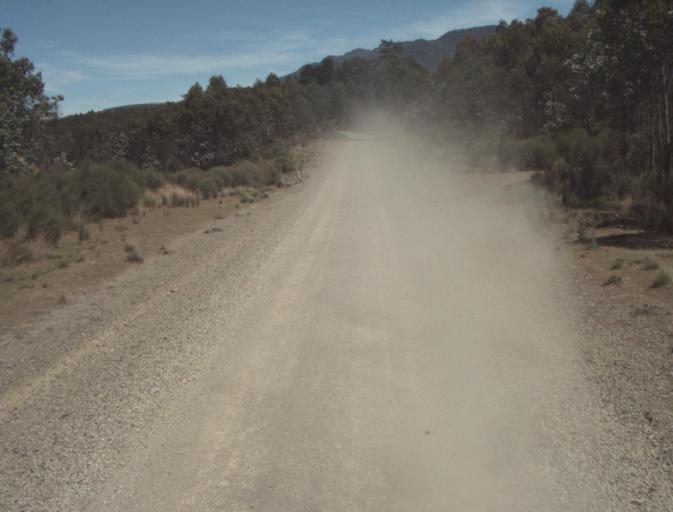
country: AU
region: Tasmania
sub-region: Dorset
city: Scottsdale
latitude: -41.3066
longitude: 147.4665
